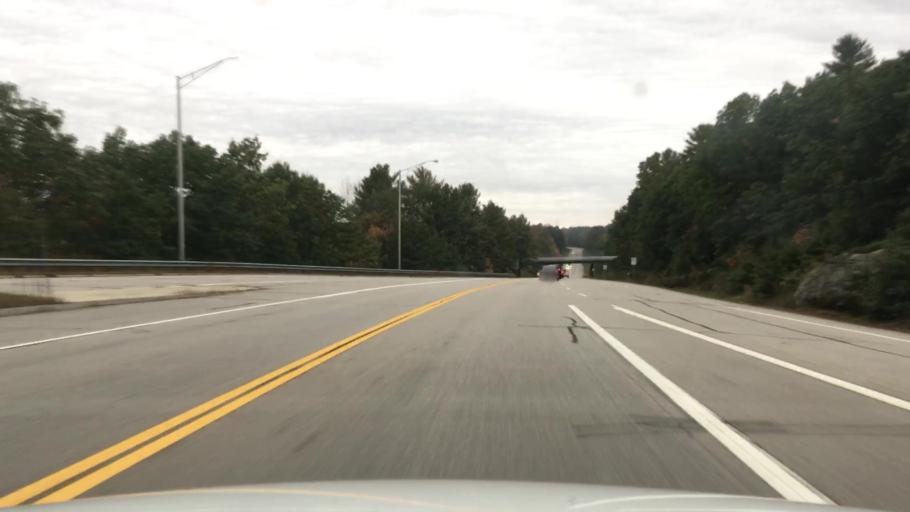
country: US
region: New Hampshire
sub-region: Strafford County
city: Durham
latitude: 43.1404
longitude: -70.9143
